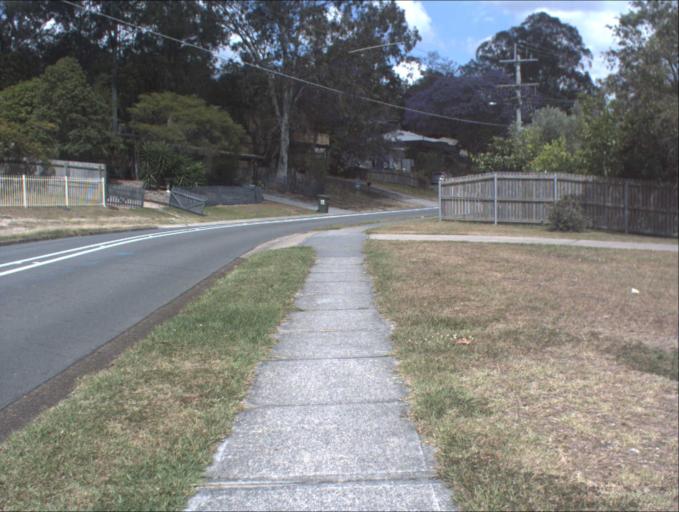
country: AU
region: Queensland
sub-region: Logan
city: Beenleigh
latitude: -27.7195
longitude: 153.1897
